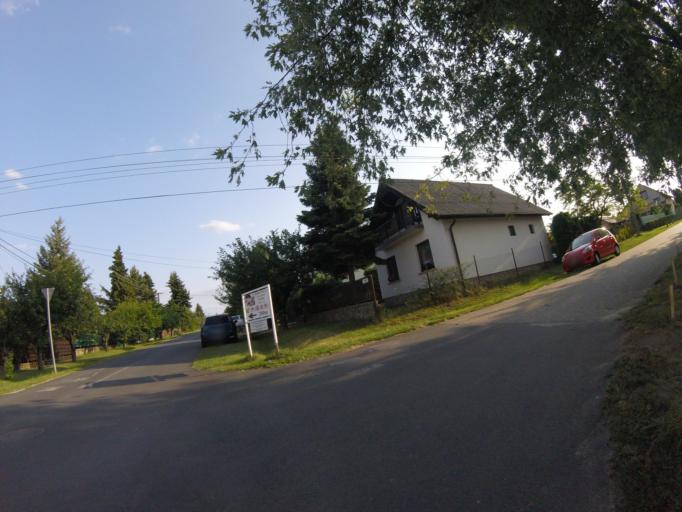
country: HU
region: Gyor-Moson-Sopron
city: Nagycenk
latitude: 47.6200
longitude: 16.7819
